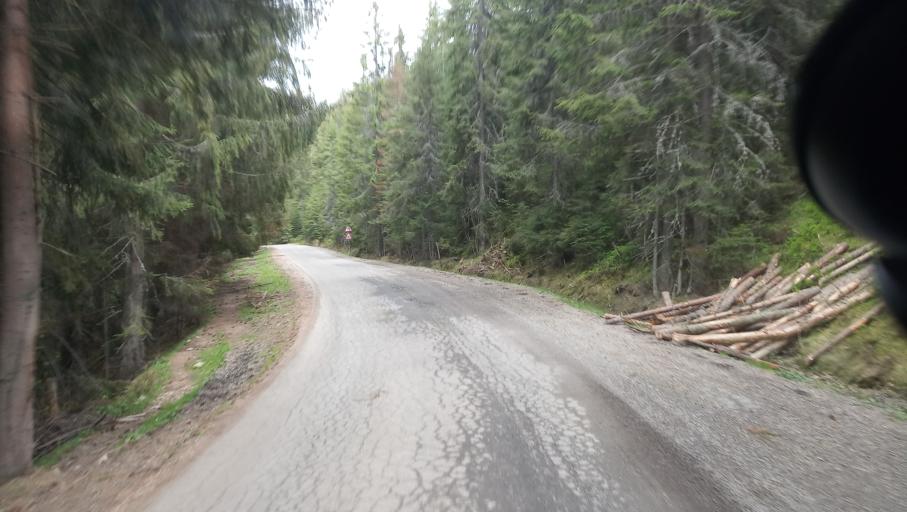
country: RO
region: Alba
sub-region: Comuna Horea
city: Horea
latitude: 46.5419
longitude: 22.8958
